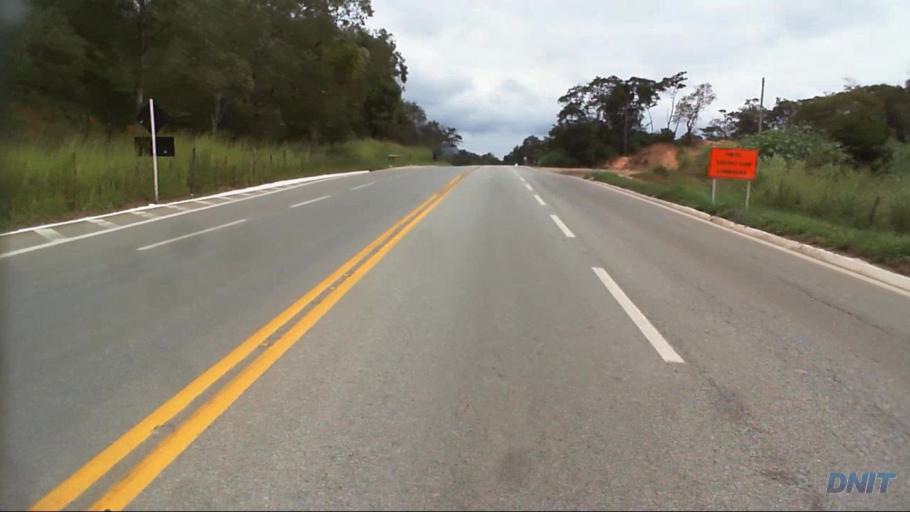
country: BR
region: Minas Gerais
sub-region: Caete
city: Caete
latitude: -19.7702
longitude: -43.6484
